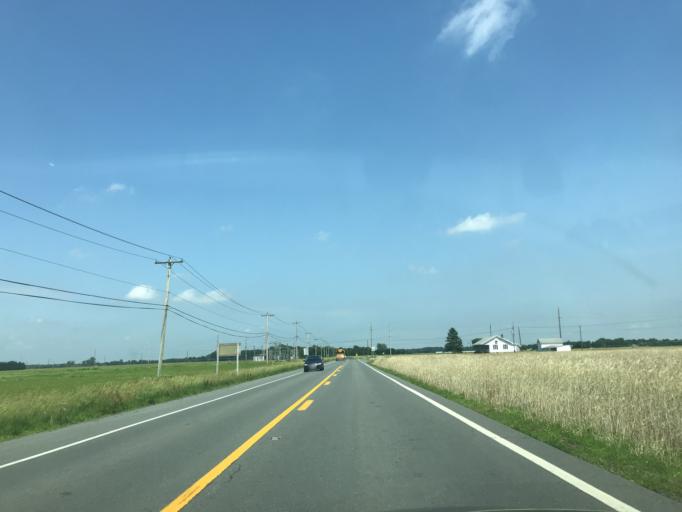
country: US
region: Maryland
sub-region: Dorchester County
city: Hurlock
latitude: 38.5969
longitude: -75.9127
